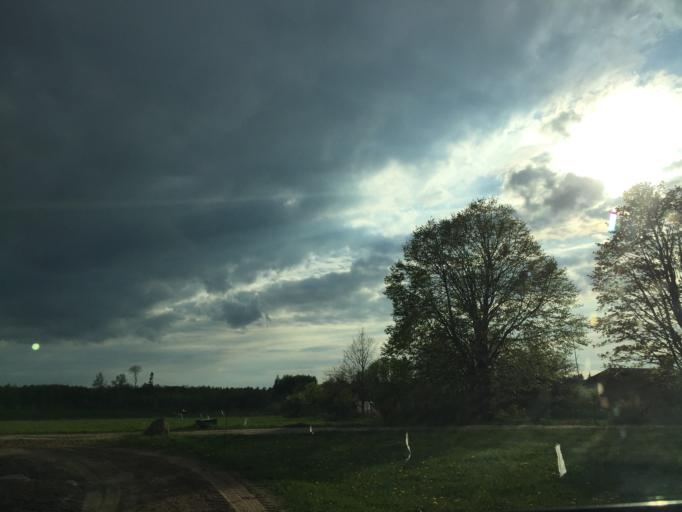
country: LV
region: Limbazu Rajons
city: Limbazi
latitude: 57.3693
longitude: 24.7645
